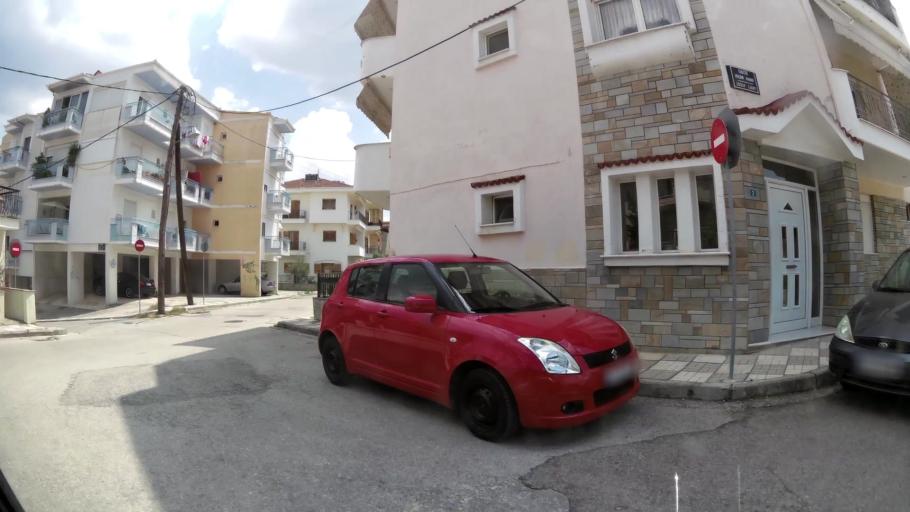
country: GR
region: West Macedonia
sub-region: Nomos Kozanis
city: Kozani
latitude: 40.2940
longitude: 21.7869
